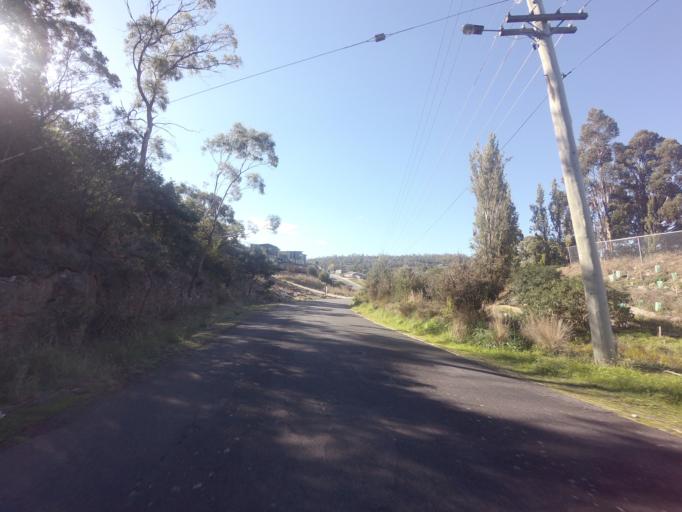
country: AU
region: Tasmania
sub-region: Clarence
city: Lindisfarne
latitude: -42.8352
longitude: 147.3469
